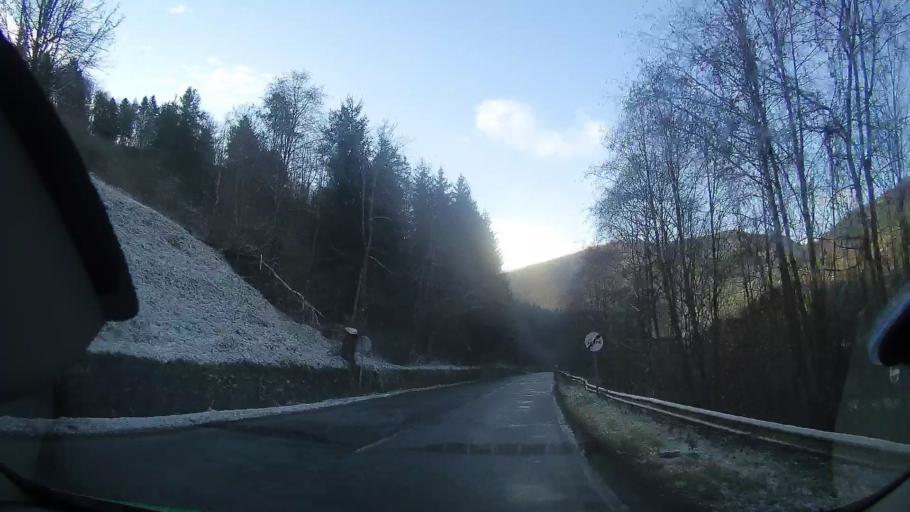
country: RO
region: Alba
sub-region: Comuna Sohodol
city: Sohodol
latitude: 46.3643
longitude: 23.0286
